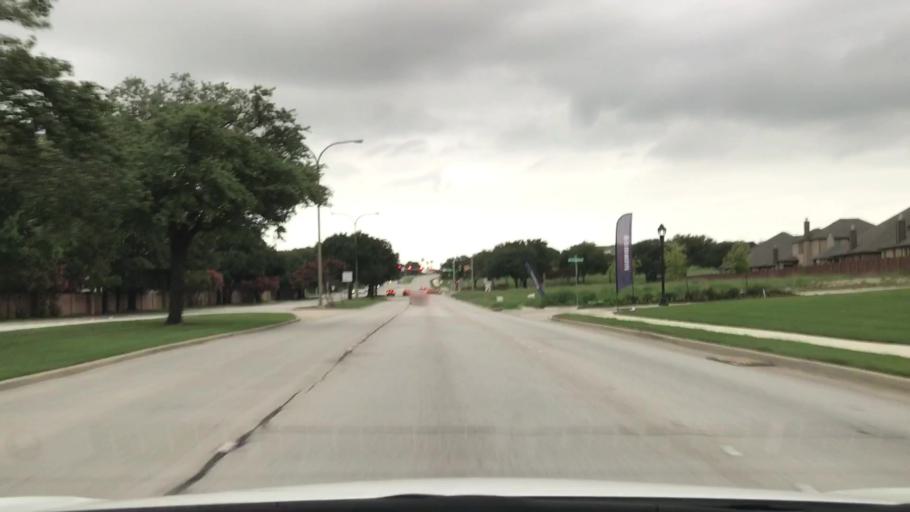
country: US
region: Texas
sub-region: Tarrant County
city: Watauga
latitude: 32.8517
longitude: -97.2901
